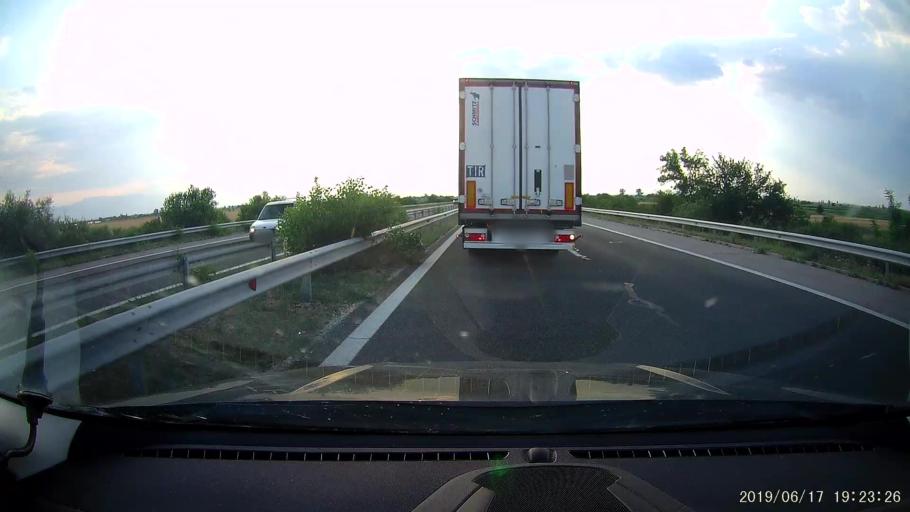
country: BG
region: Pazardzhik
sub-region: Obshtina Pazardzhik
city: Pazardzhik
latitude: 42.2191
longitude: 24.4048
